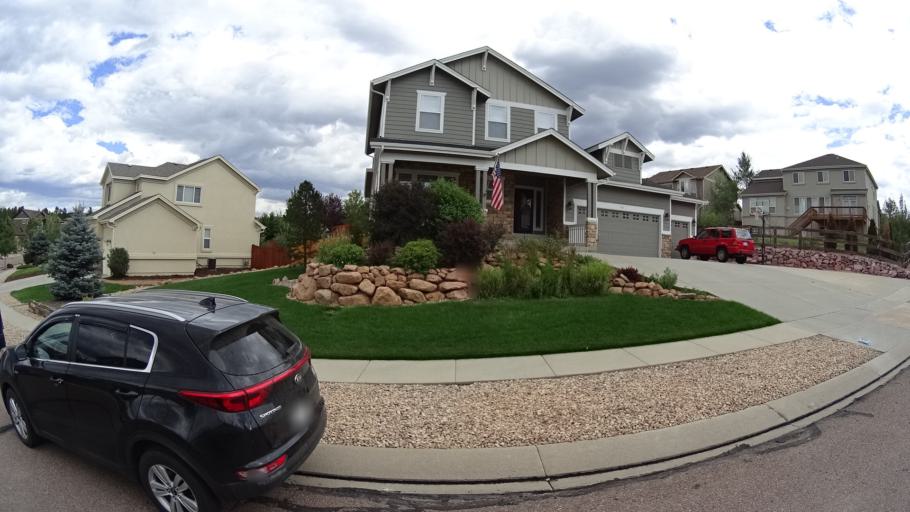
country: US
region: Colorado
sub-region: El Paso County
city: Gleneagle
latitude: 39.0330
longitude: -104.8164
